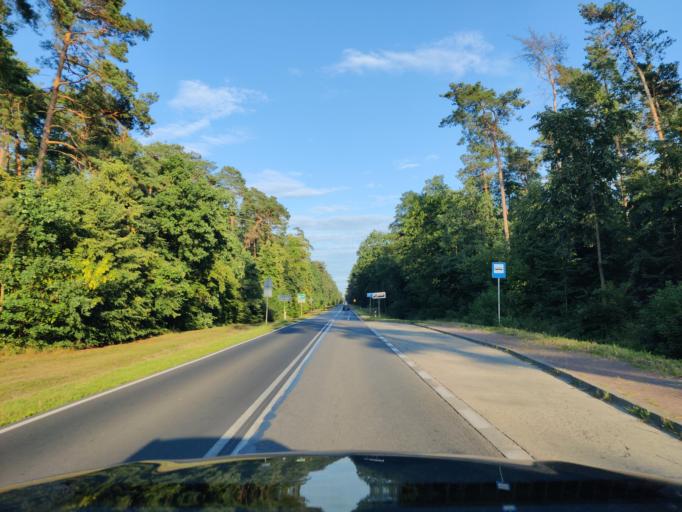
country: PL
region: Masovian Voivodeship
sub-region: Powiat pultuski
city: Pultusk
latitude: 52.6814
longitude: 21.1270
